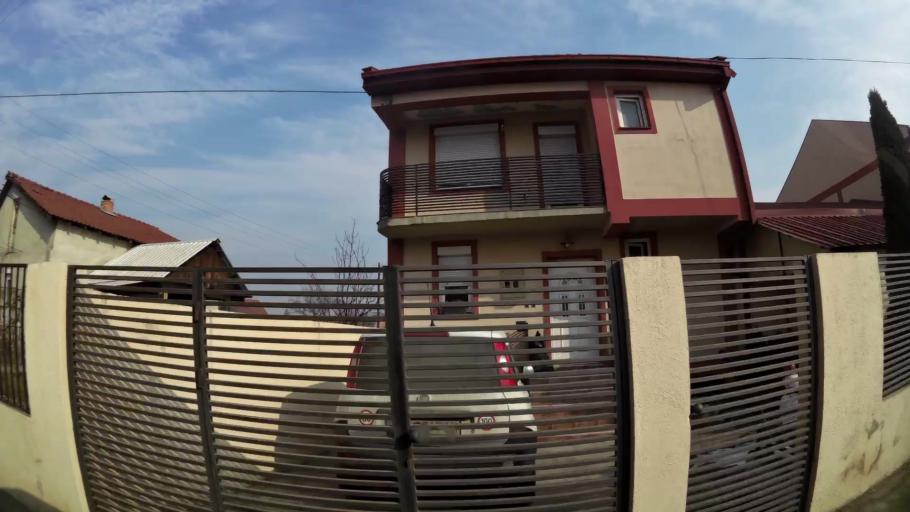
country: MK
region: Kisela Voda
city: Kisela Voda
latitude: 41.9904
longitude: 21.5001
